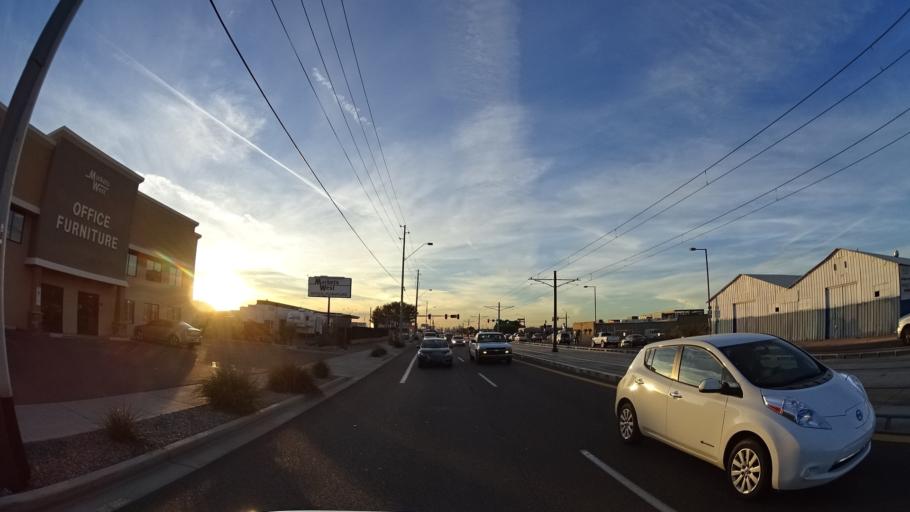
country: US
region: Arizona
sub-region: Maricopa County
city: Tempe Junction
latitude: 33.4480
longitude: -111.9942
